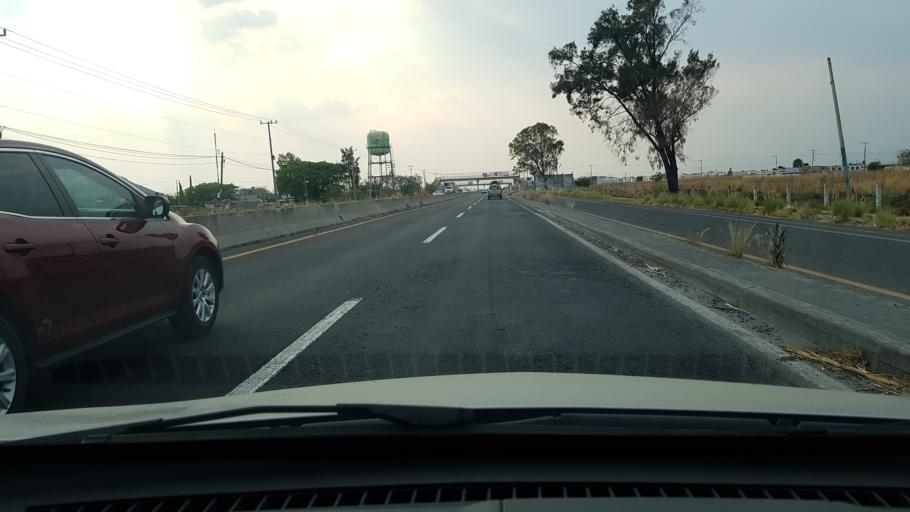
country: MX
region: Morelos
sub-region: Ayala
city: Unidad Habitacional Mariano Matamoros
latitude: 18.7495
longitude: -98.8489
